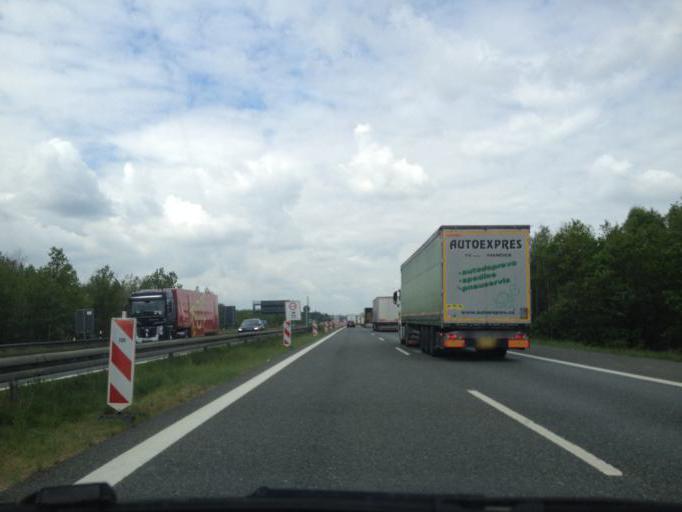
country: DE
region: Bavaria
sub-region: Regierungsbezirk Mittelfranken
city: Feucht
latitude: 49.3965
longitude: 11.2038
